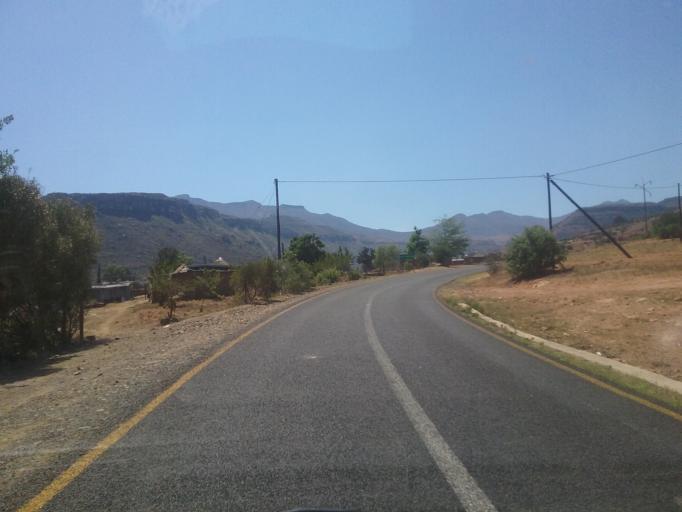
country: LS
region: Quthing
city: Quthing
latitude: -30.3378
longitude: 27.7373
